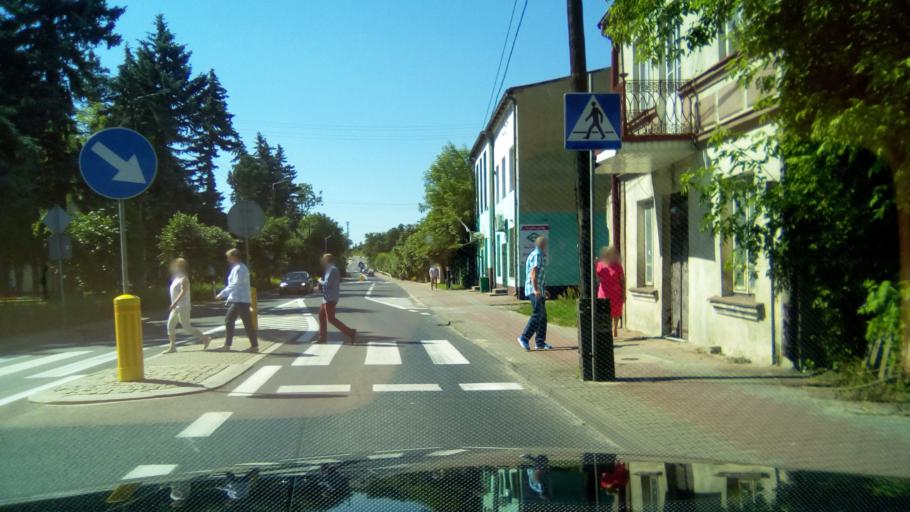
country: PL
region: Lodz Voivodeship
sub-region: Powiat tomaszowski
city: Inowlodz
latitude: 51.5233
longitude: 20.2232
